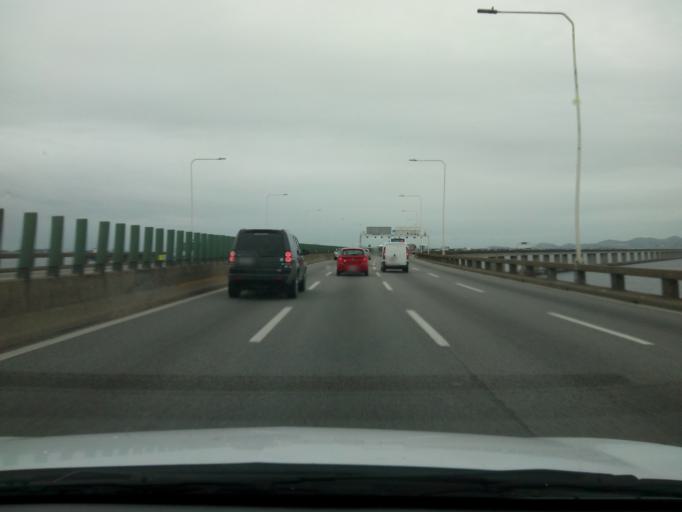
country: BR
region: Rio de Janeiro
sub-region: Rio De Janeiro
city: Rio de Janeiro
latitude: -22.8690
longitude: -43.2010
